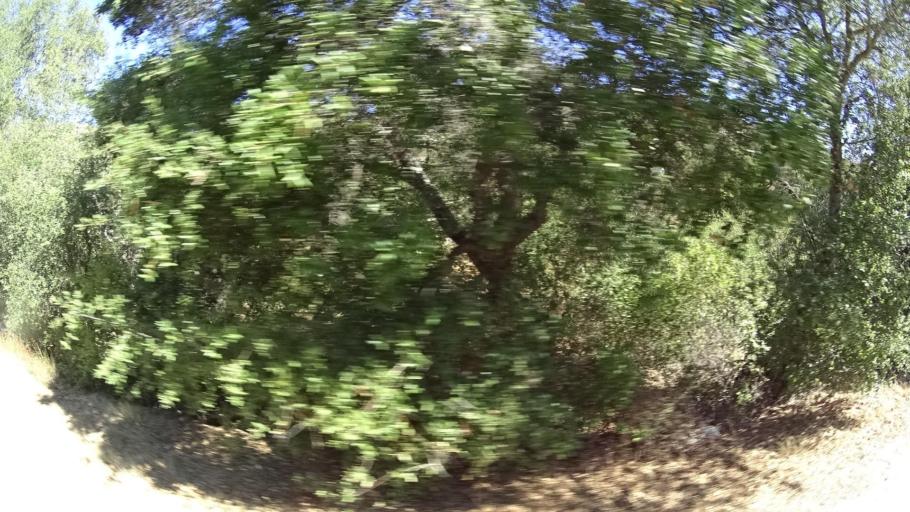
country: US
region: California
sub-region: San Diego County
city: Alpine
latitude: 32.7073
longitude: -116.7368
